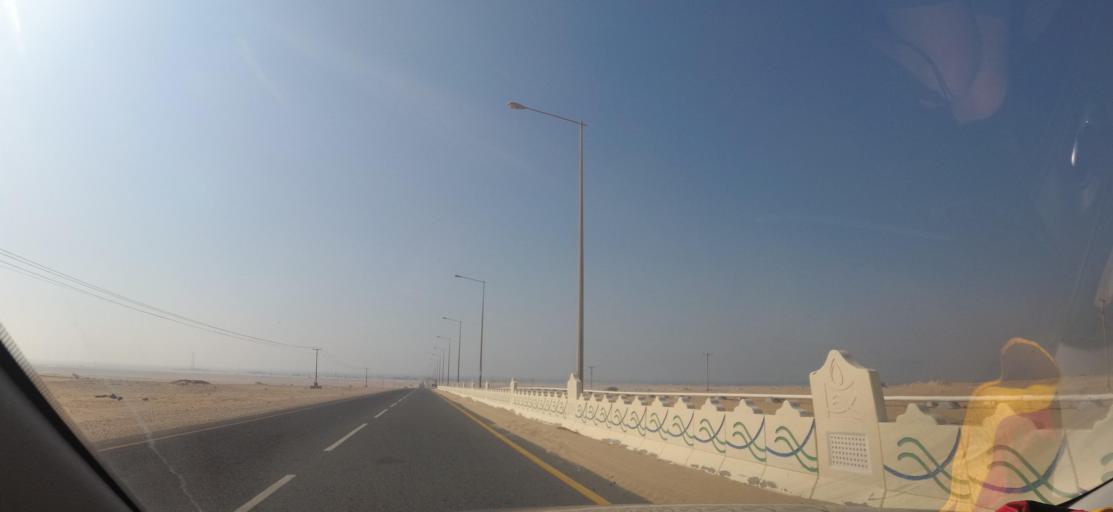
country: QA
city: Umm Bab
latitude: 25.2125
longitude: 50.7869
